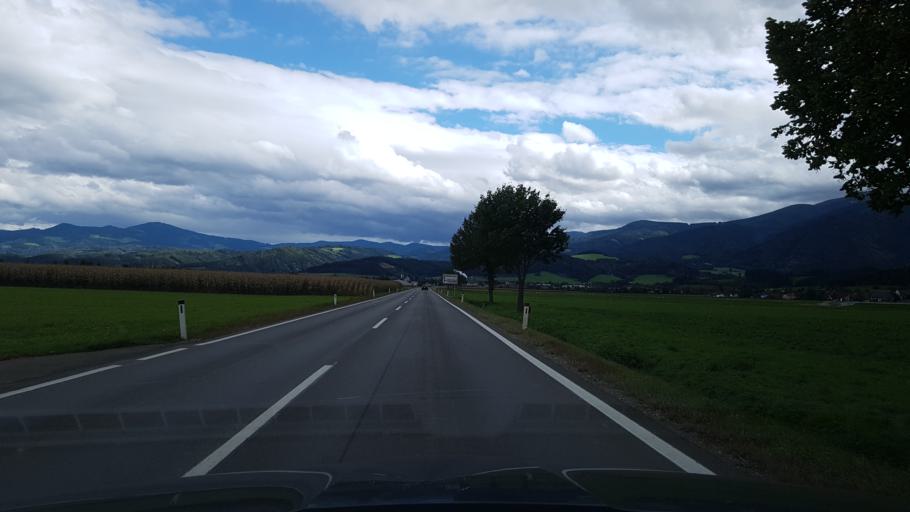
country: AT
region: Styria
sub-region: Politischer Bezirk Murtal
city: Weisskirchen in Steiermark
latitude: 47.1623
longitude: 14.7032
